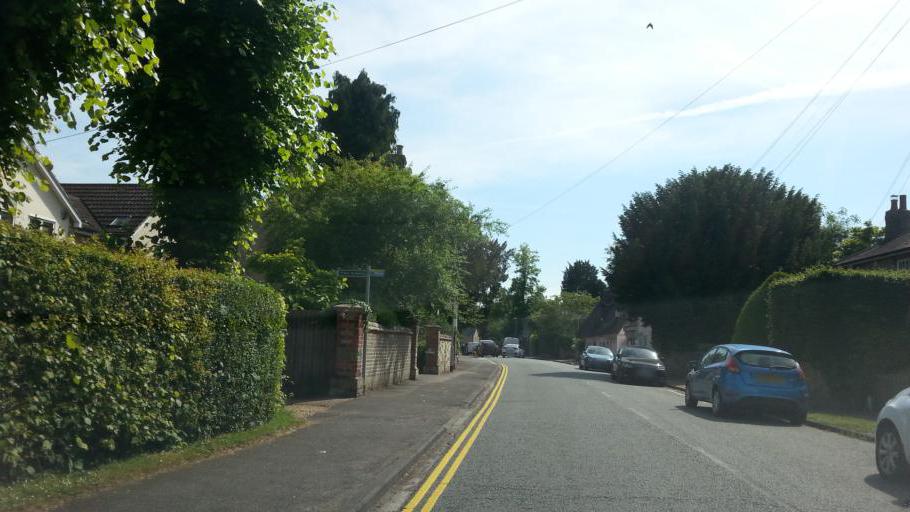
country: GB
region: England
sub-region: Cambridgeshire
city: Sawston
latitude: 52.1486
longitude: 0.1339
